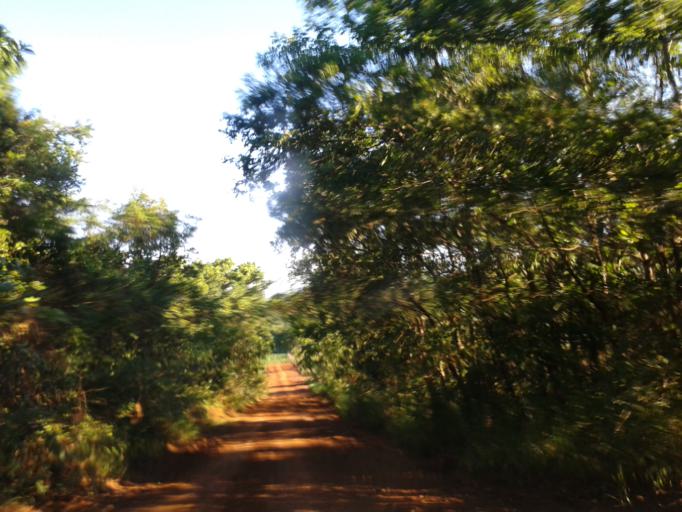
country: BR
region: Minas Gerais
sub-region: Centralina
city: Centralina
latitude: -18.6944
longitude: -49.2788
